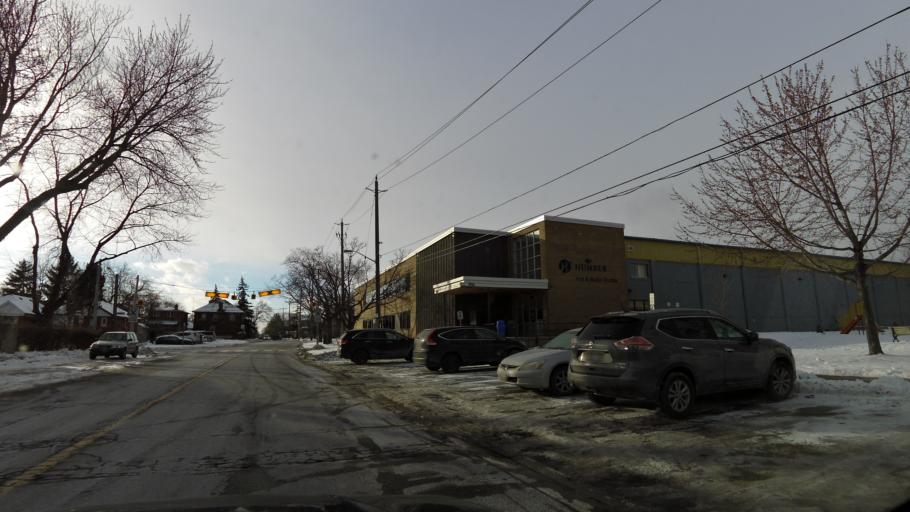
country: CA
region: Ontario
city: Etobicoke
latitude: 43.6002
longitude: -79.5206
